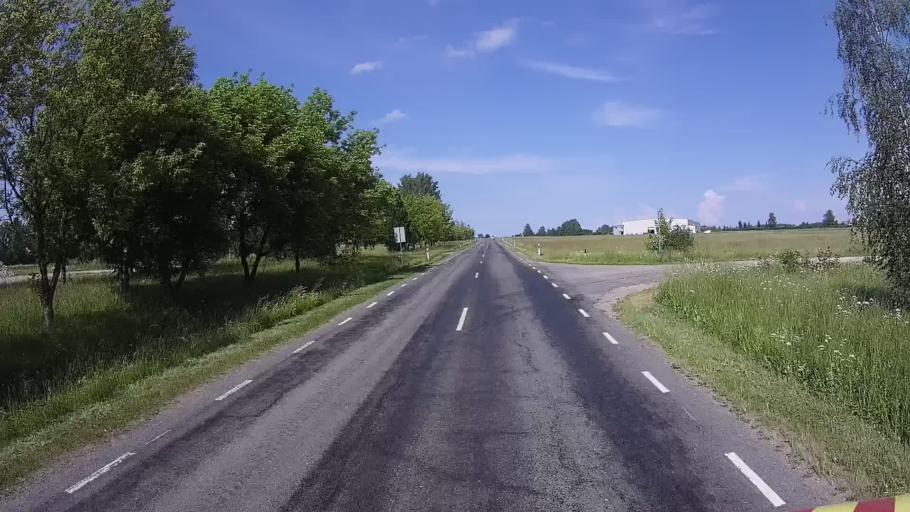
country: EE
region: Viljandimaa
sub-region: Karksi vald
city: Karksi-Nuia
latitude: 58.0919
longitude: 25.5586
